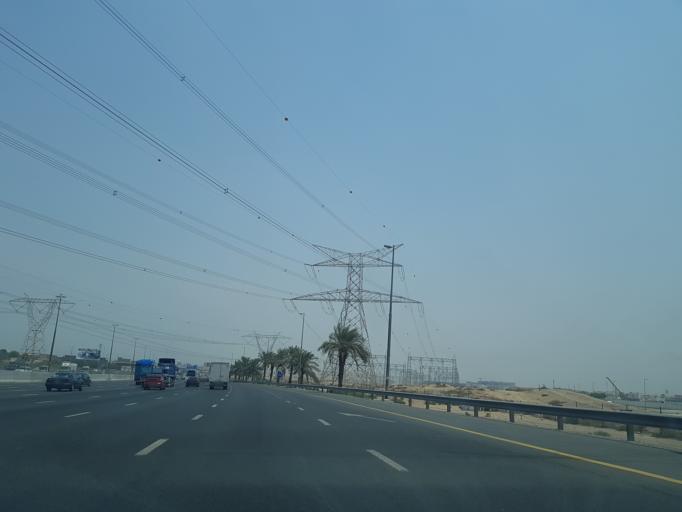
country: AE
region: Ash Shariqah
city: Sharjah
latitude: 25.2200
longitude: 55.4054
